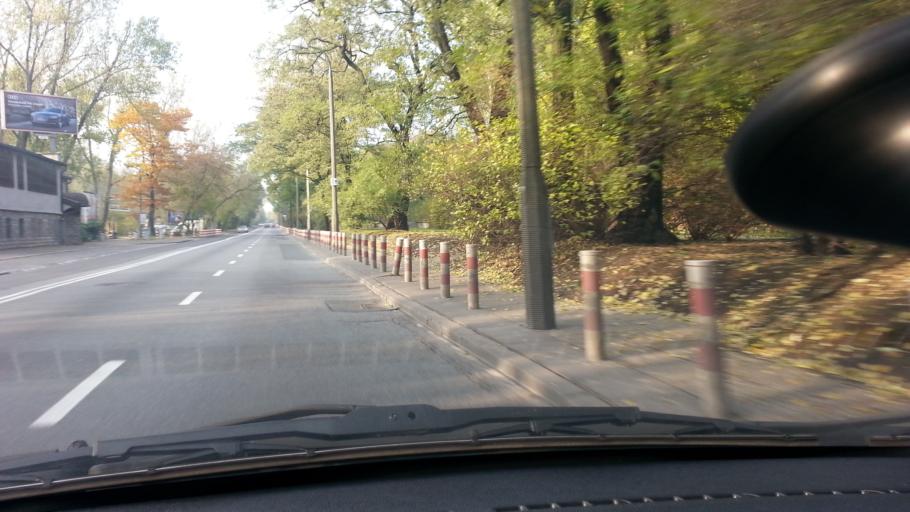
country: PL
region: Masovian Voivodeship
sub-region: Warszawa
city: Praga Polnoc
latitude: 52.2544
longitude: 21.0216
